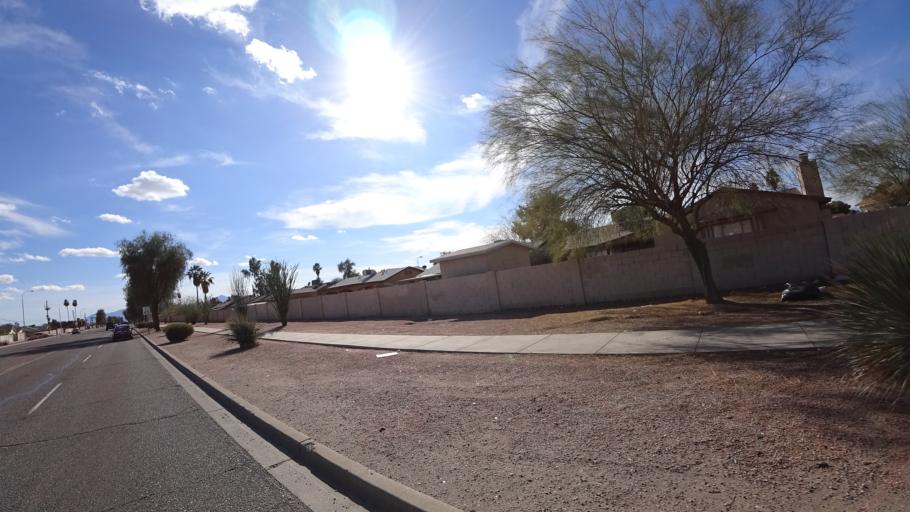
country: US
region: Arizona
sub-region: Maricopa County
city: Glendale
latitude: 33.5046
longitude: -112.2206
